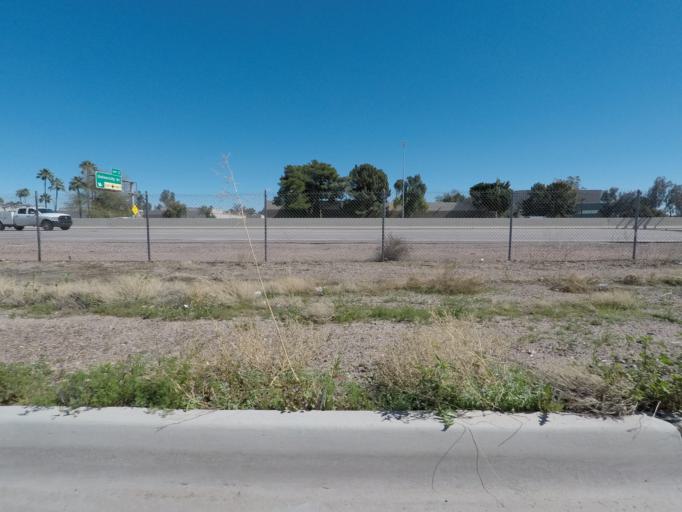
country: US
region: Arizona
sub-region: Maricopa County
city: Tempe Junction
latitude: 33.4143
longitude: -111.9786
